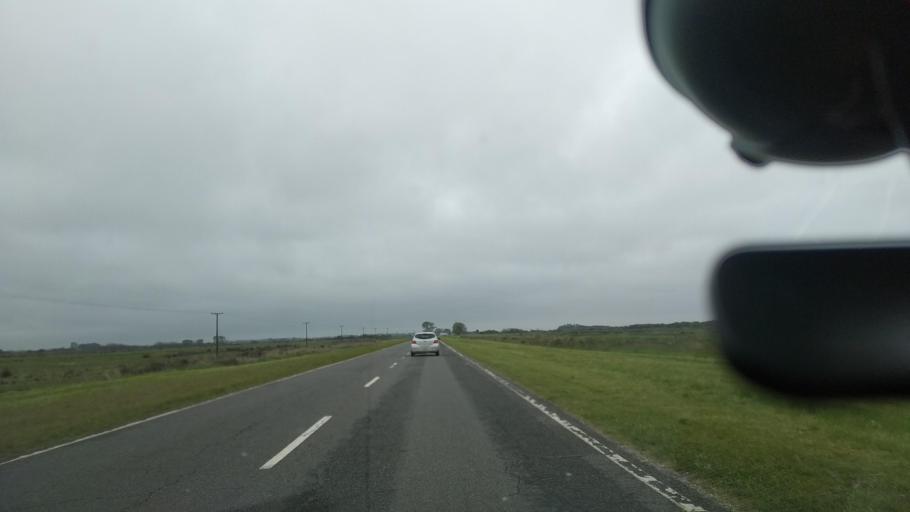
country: AR
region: Buenos Aires
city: Veronica
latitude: -35.6008
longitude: -57.2759
